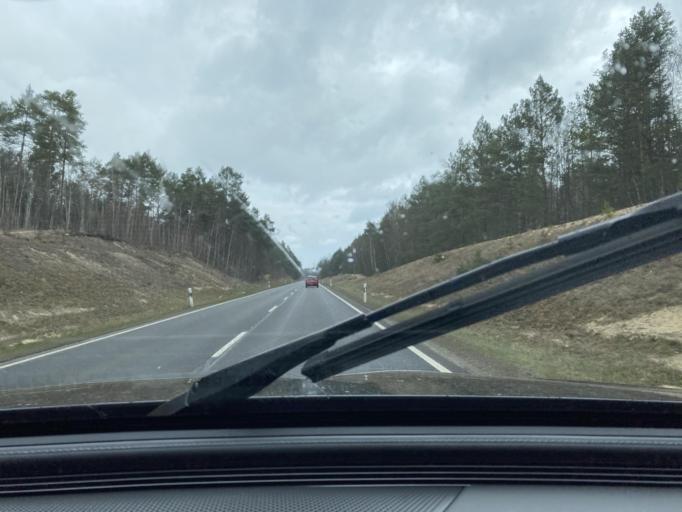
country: DE
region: Saxony
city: Weisskeissel
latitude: 51.4471
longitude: 14.6761
